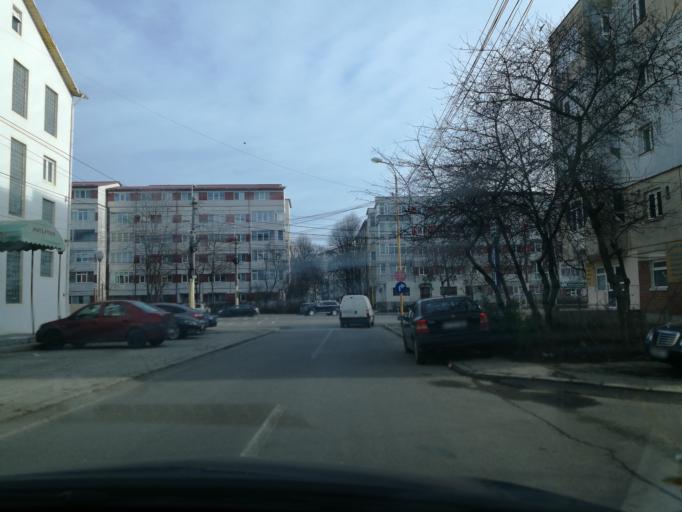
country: RO
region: Constanta
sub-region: Municipiul Constanta
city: Constanta
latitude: 44.1789
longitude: 28.6154
